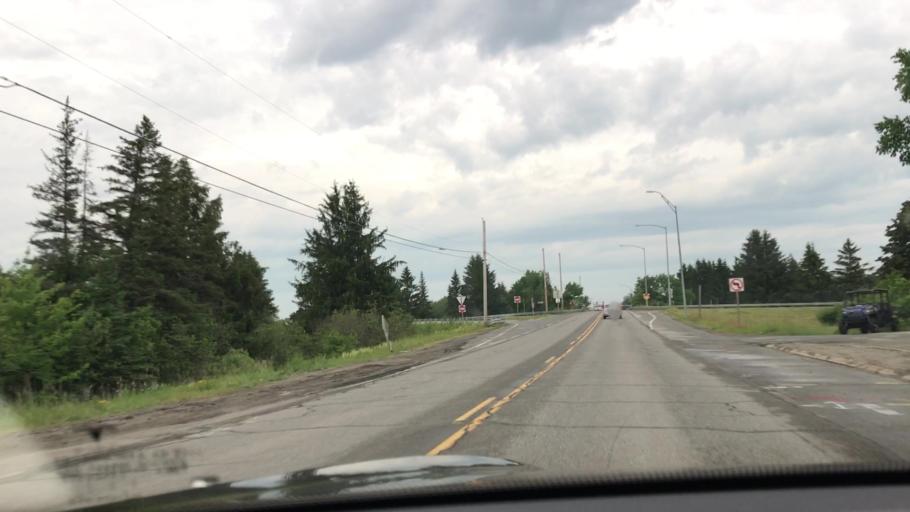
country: US
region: Maine
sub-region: Penobscot County
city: Orono
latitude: 44.9010
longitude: -68.6935
